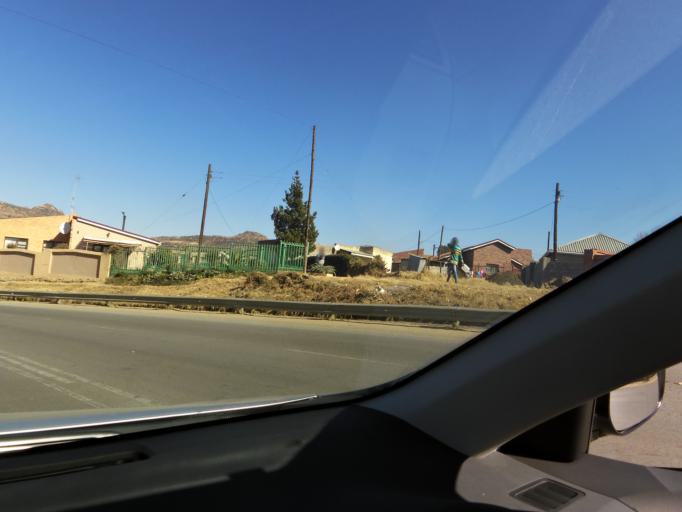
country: LS
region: Maseru
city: Maseru
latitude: -29.3162
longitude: 27.5096
